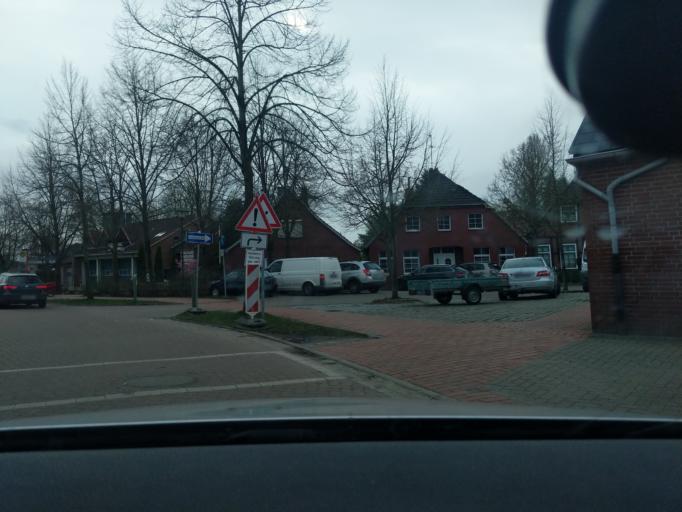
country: DE
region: Lower Saxony
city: Horneburg
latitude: 53.5088
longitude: 9.5853
